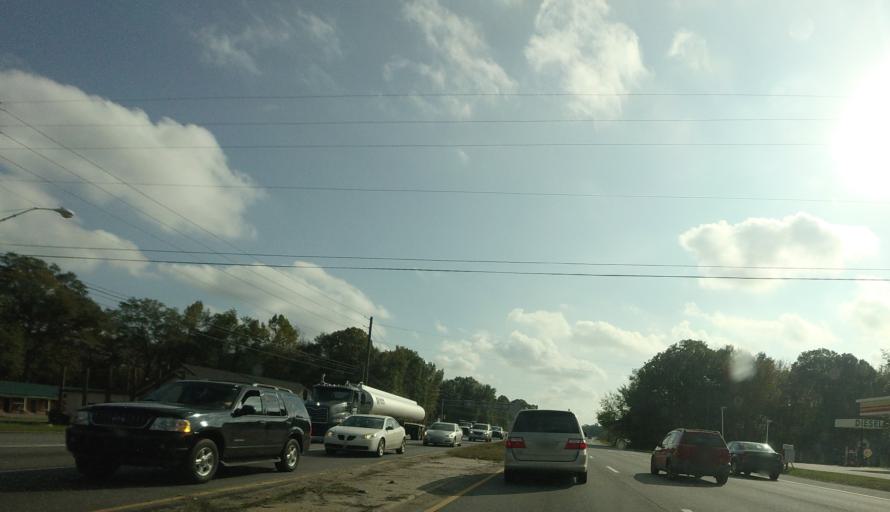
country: US
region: Georgia
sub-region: Bibb County
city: Macon
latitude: 32.7716
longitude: -83.6595
